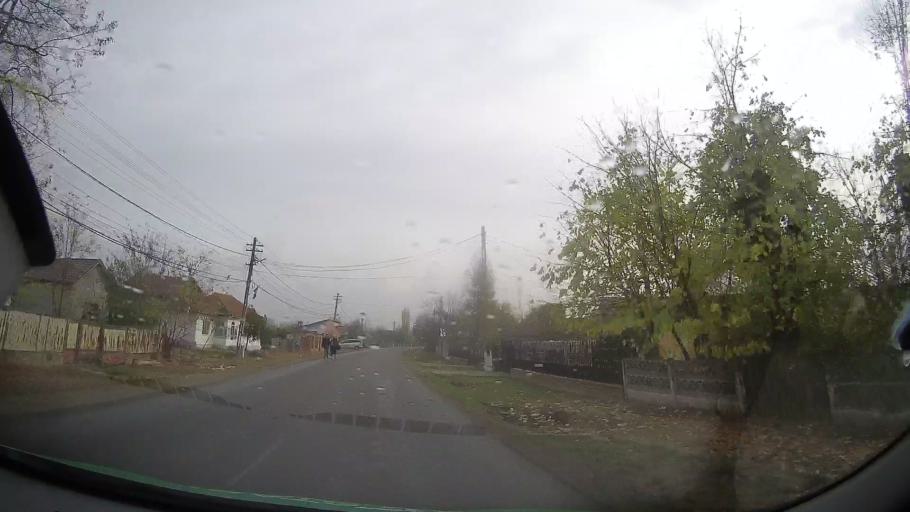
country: RO
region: Prahova
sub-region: Comuna Rafov
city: Palanca
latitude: 44.8444
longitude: 26.2339
